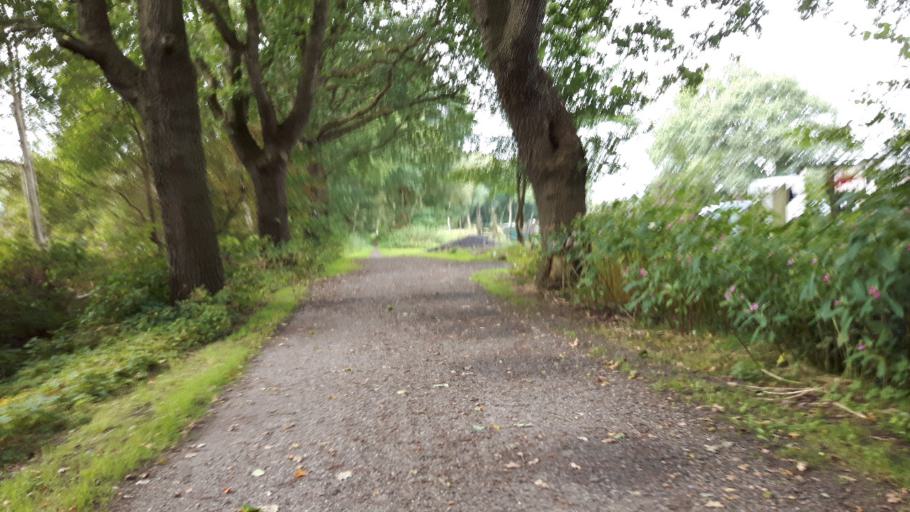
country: NL
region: Groningen
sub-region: Gemeente Leek
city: Leek
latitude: 53.1128
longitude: 6.4263
